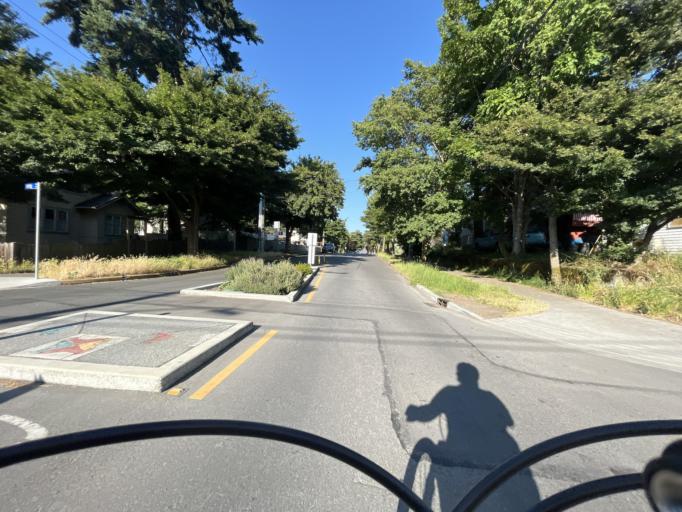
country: CA
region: British Columbia
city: Victoria
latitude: 48.4376
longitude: -123.3573
